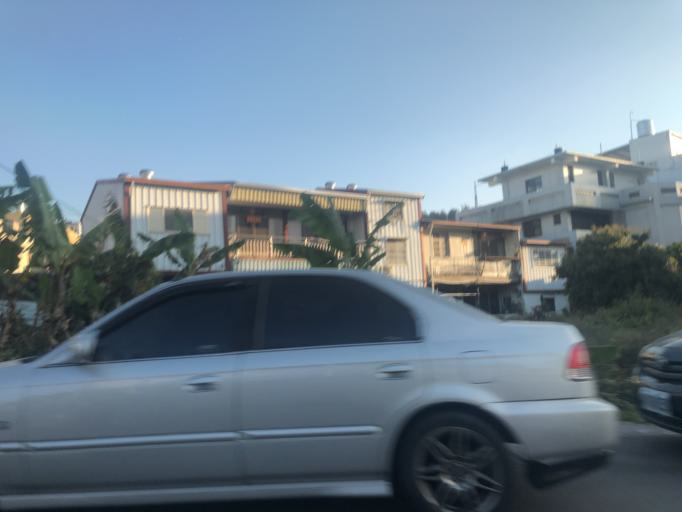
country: TW
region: Taiwan
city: Fengyuan
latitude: 24.2772
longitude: 120.7728
